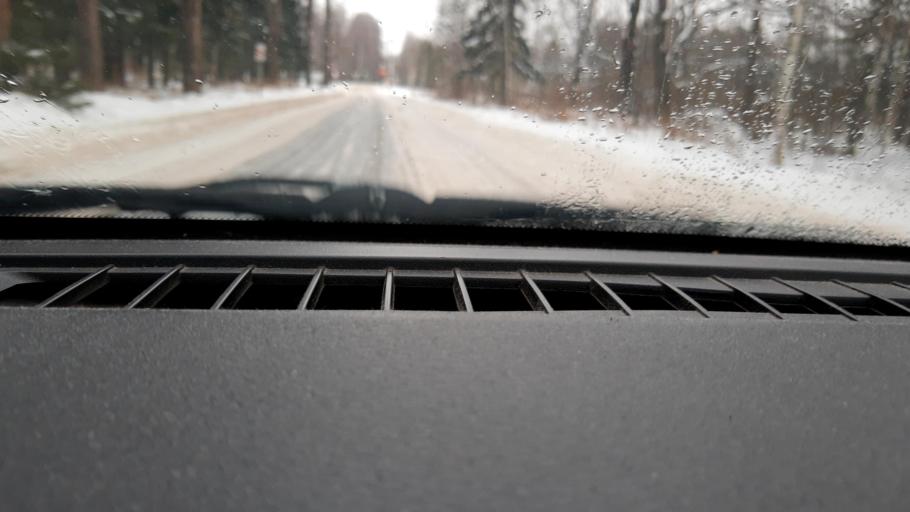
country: RU
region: Nizjnij Novgorod
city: Afonino
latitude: 56.1869
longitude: 44.0790
